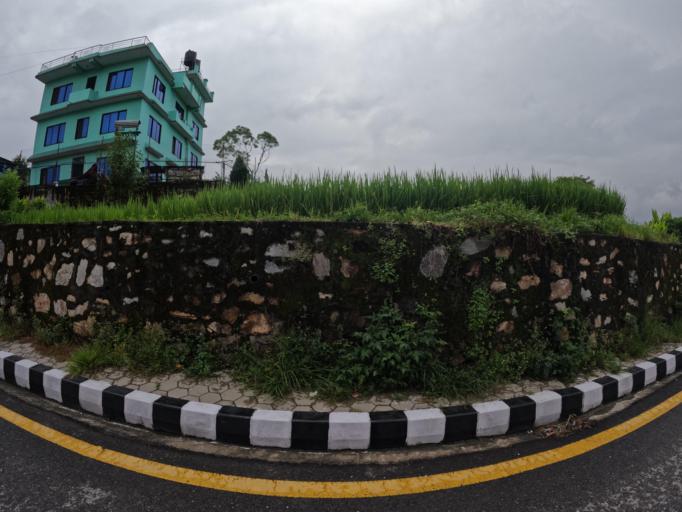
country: NP
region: Central Region
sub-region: Bagmati Zone
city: Kathmandu
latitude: 27.7606
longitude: 85.3277
